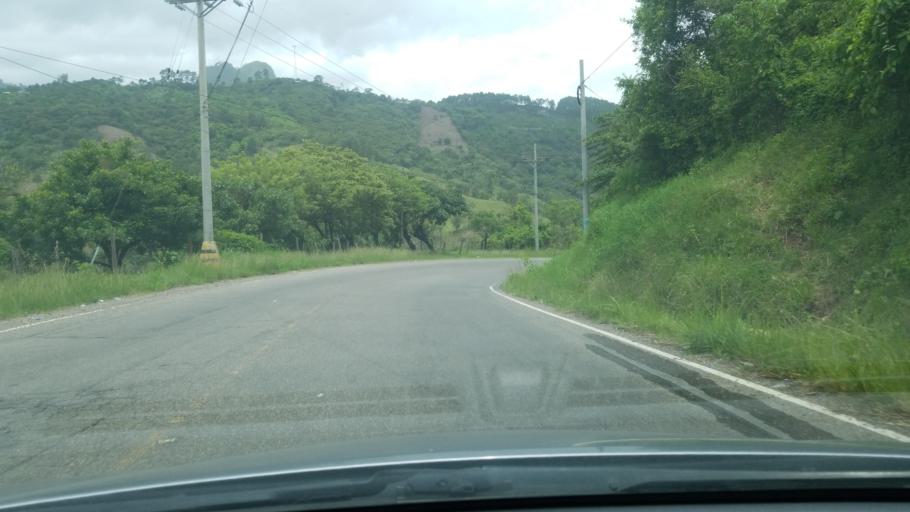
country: HN
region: Copan
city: Ojos de Agua
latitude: 14.6753
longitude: -88.8198
